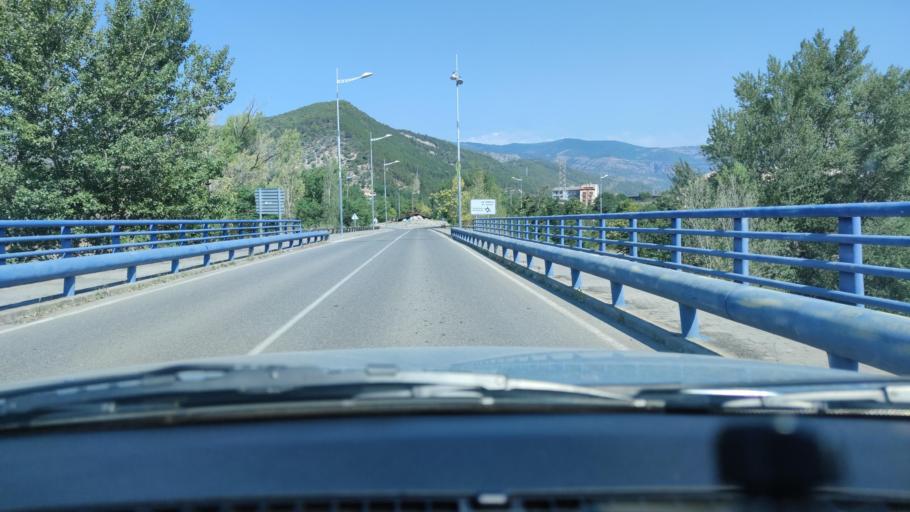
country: ES
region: Catalonia
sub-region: Provincia de Lleida
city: Senterada
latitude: 42.2430
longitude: 0.9702
